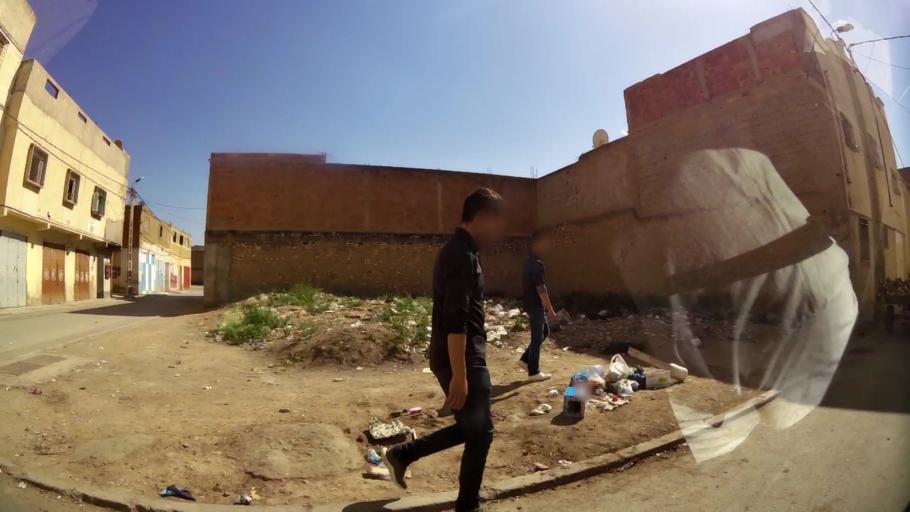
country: MA
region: Oriental
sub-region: Oujda-Angad
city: Oujda
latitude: 34.6827
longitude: -1.9272
